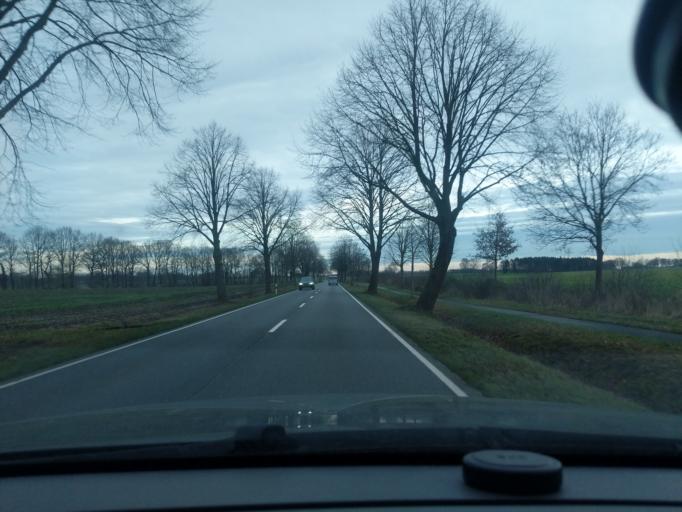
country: DE
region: Lower Saxony
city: Sauensiek
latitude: 53.3936
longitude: 9.6067
